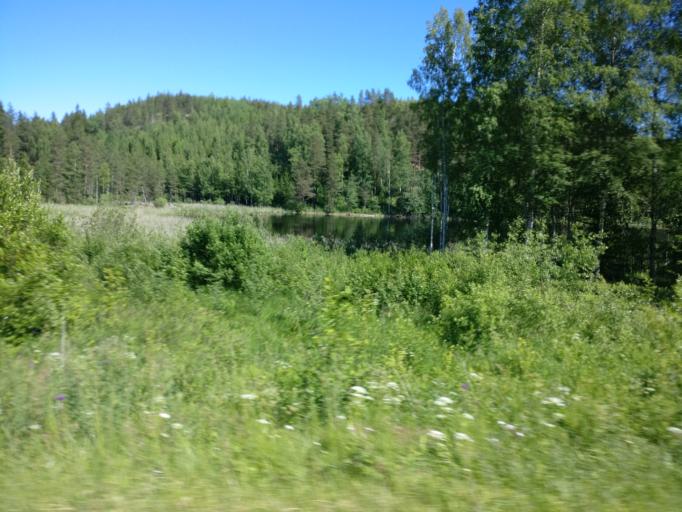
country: FI
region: Southern Savonia
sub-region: Savonlinna
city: Rantasalmi
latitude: 62.1215
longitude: 28.2638
